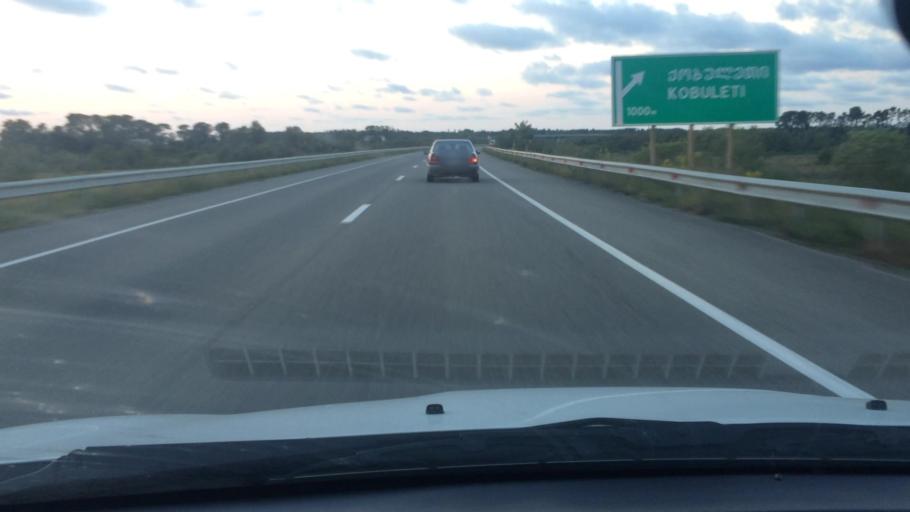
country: GE
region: Guria
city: Urek'i
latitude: 41.9115
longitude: 41.7812
